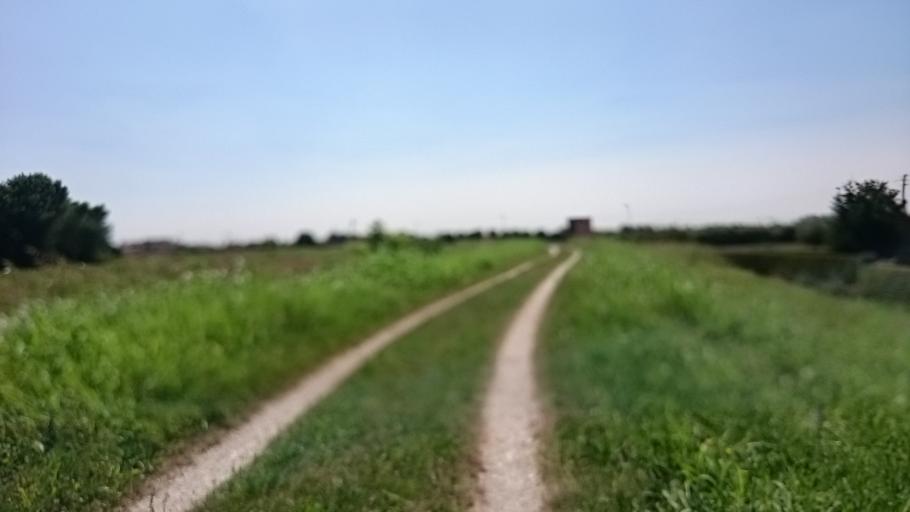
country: IT
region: Veneto
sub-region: Provincia di Padova
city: Saccolongo
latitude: 45.3947
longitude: 11.7702
